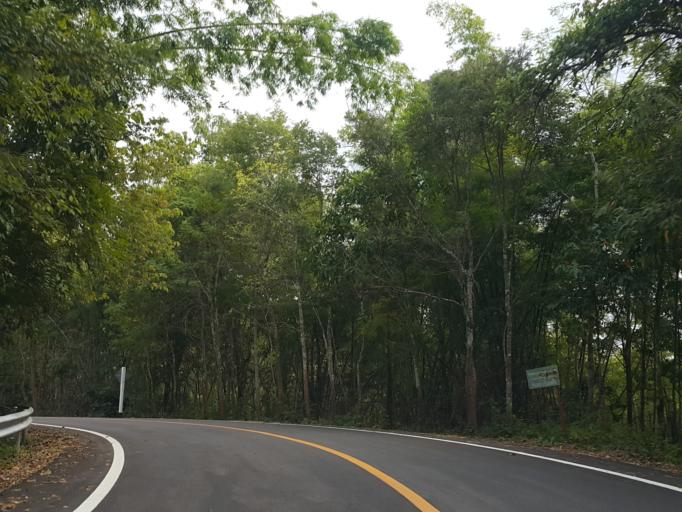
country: TH
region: Lampang
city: Chae Hom
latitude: 18.6518
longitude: 99.5227
